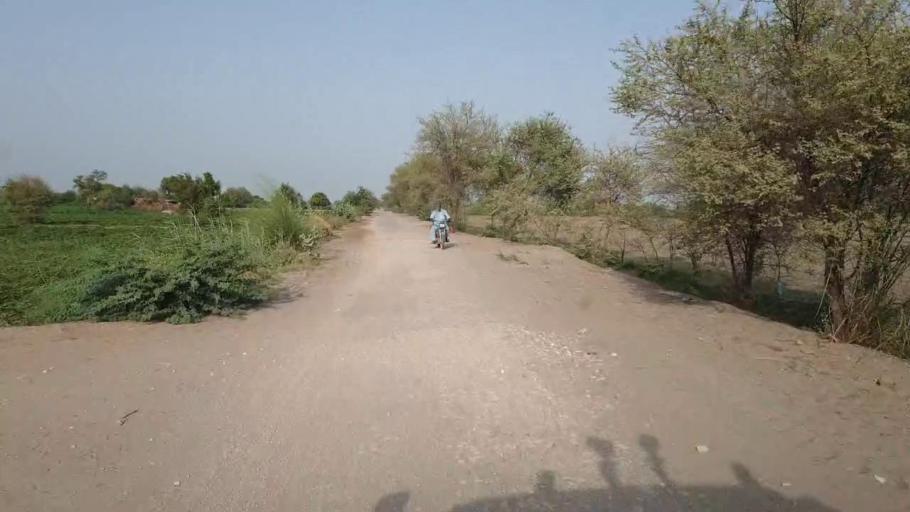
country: PK
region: Sindh
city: Daur
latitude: 26.3432
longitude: 68.2660
